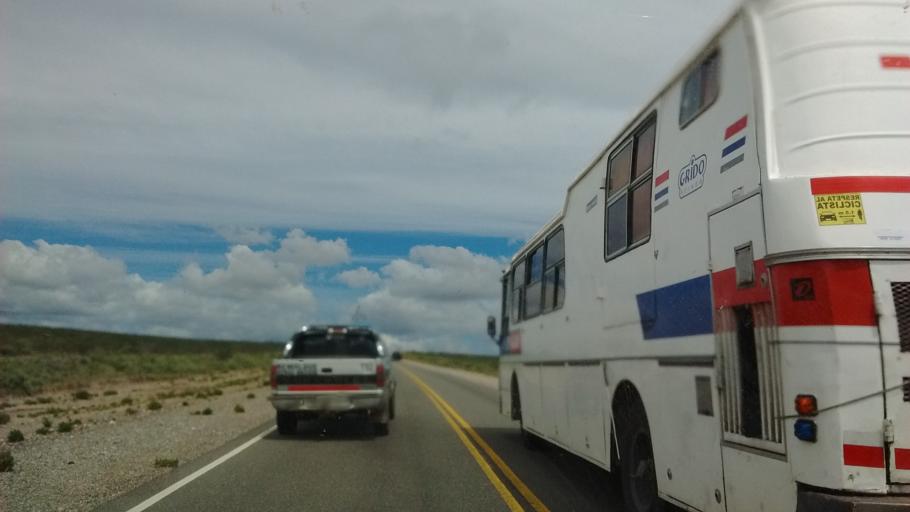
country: AR
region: Neuquen
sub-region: Departamento de Picun Leufu
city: Picun Leufu
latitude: -39.7336
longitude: -69.5852
